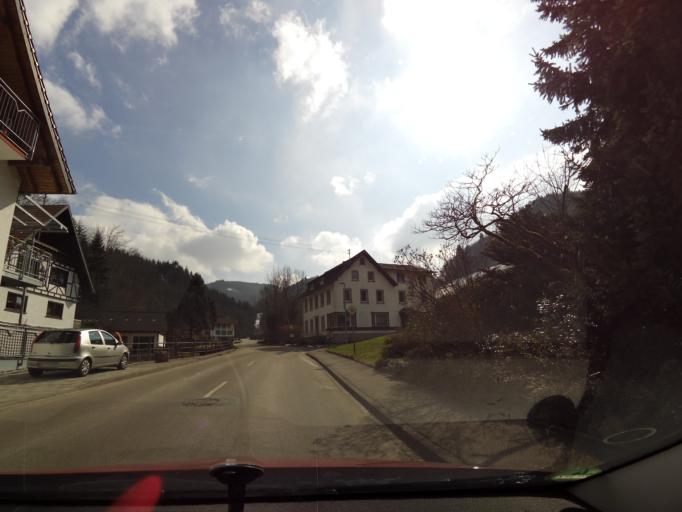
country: DE
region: Baden-Wuerttemberg
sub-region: Freiburg Region
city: Ottenhofen im Schwarzwald
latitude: 48.5557
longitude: 8.1552
